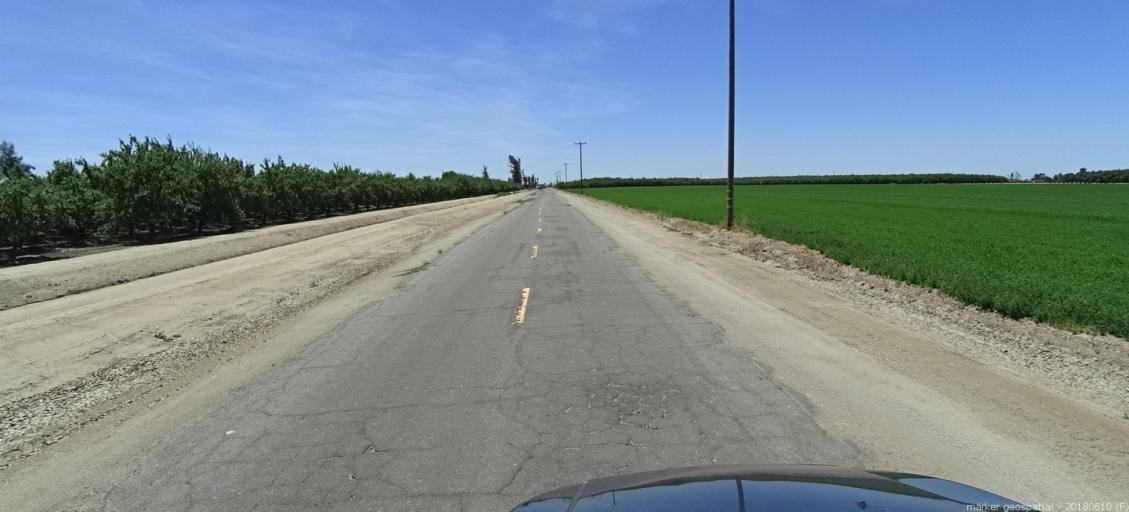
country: US
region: California
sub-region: Madera County
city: Chowchilla
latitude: 37.0688
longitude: -120.3782
